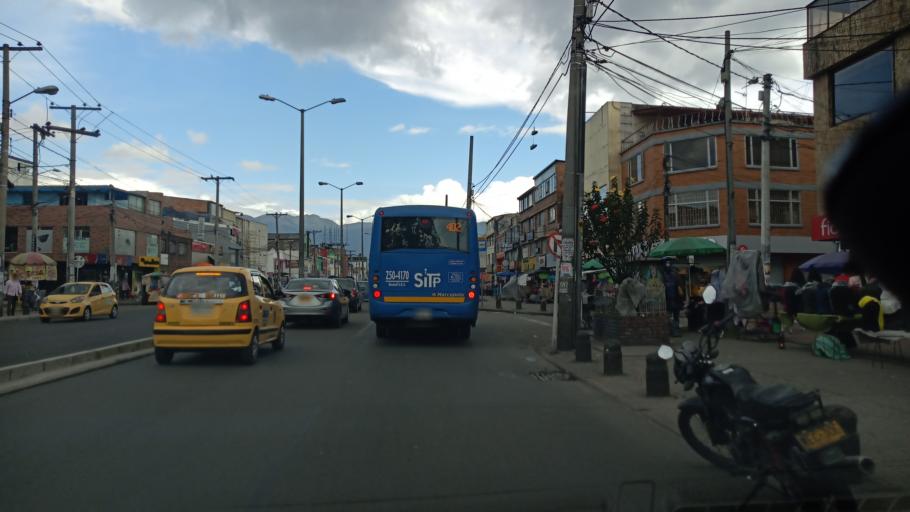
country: CO
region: Bogota D.C.
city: Barrio San Luis
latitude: 4.6828
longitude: -74.0906
